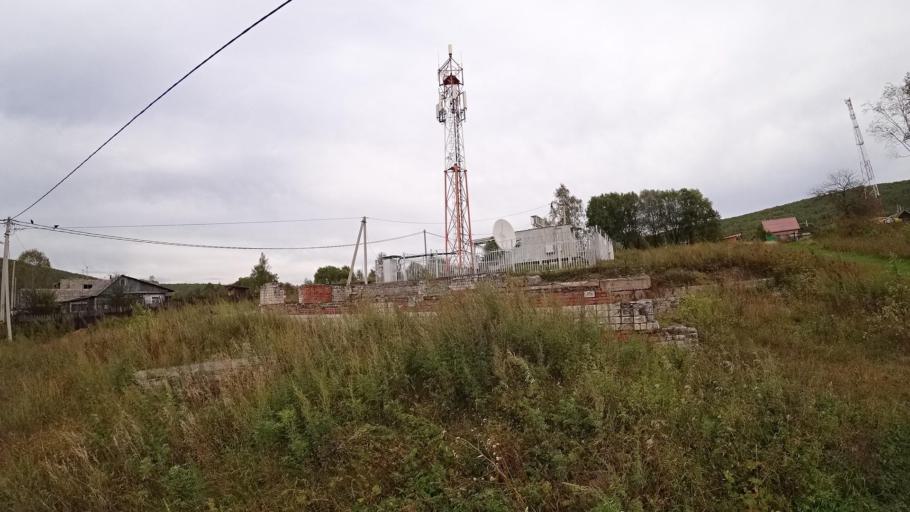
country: RU
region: Jewish Autonomous Oblast
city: Khingansk
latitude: 49.1269
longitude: 131.2044
